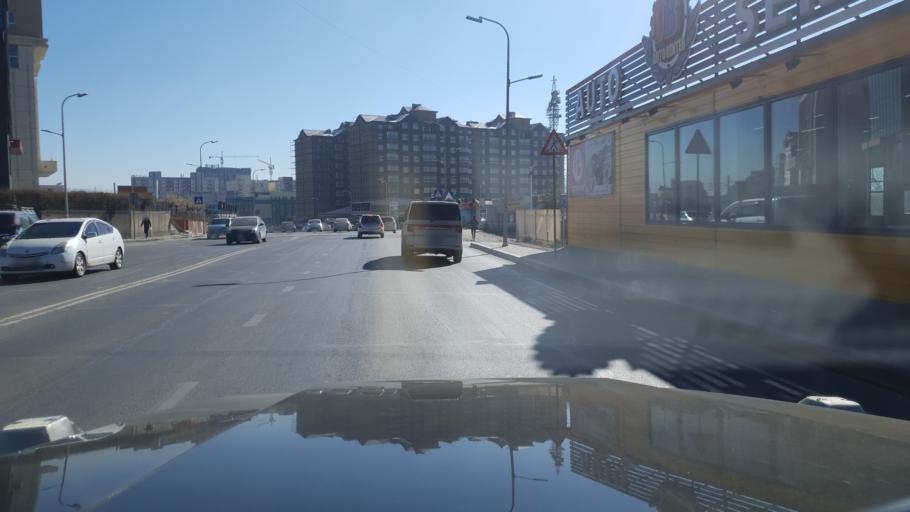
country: MN
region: Ulaanbaatar
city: Ulaanbaatar
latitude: 47.9245
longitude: 106.9475
